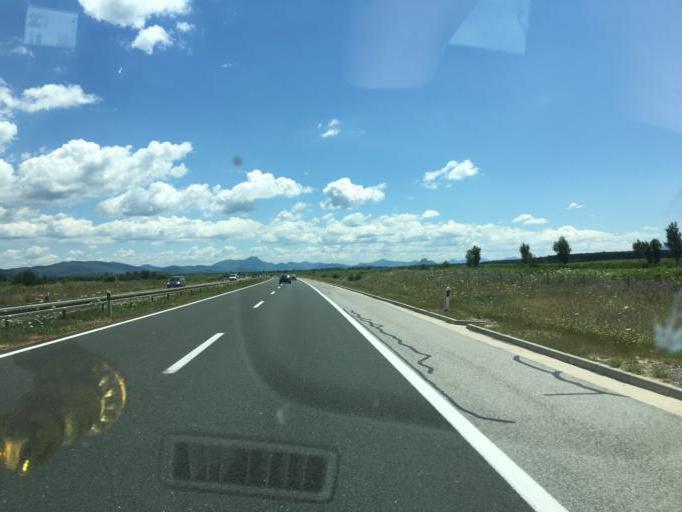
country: HR
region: Licko-Senjska
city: Gospic
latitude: 44.5212
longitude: 15.4642
